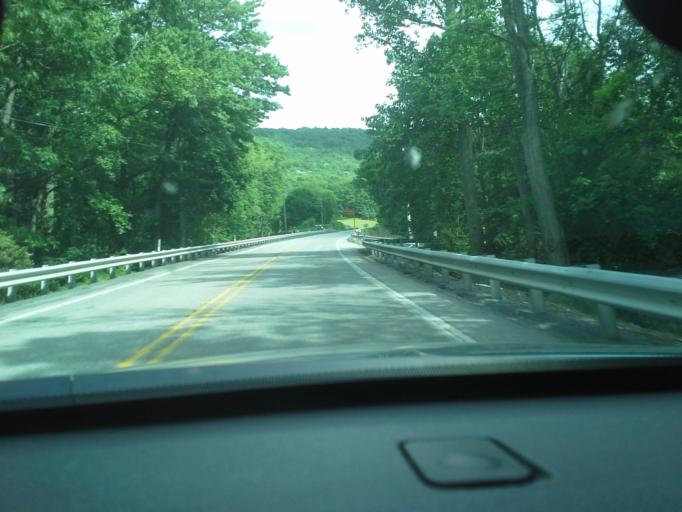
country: US
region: Pennsylvania
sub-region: Fulton County
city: McConnellsburg
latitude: 39.9164
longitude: -77.9704
